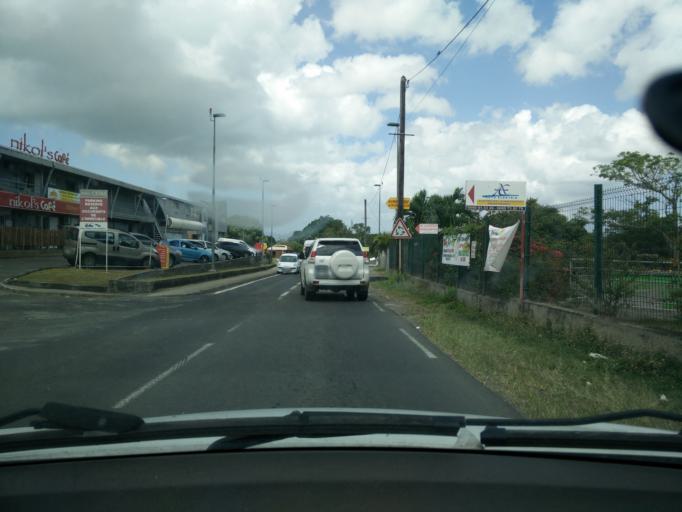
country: GP
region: Guadeloupe
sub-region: Guadeloupe
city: Les Abymes
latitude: 16.2592
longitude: -61.5102
